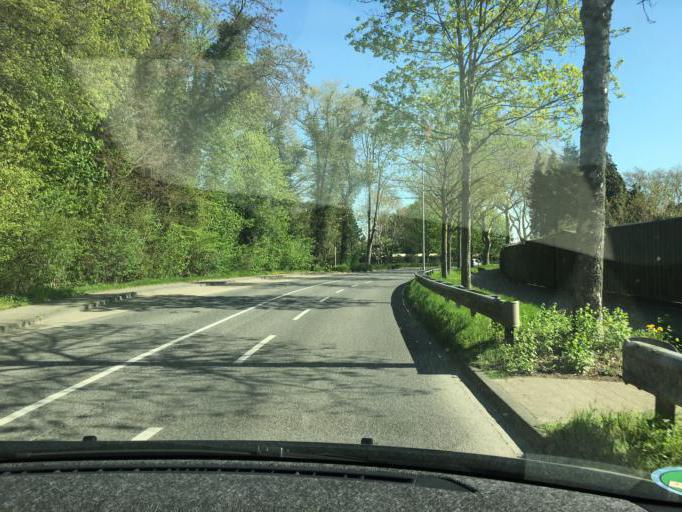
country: DE
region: North Rhine-Westphalia
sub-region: Regierungsbezirk Dusseldorf
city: Monchengladbach
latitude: 51.1384
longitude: 6.4082
